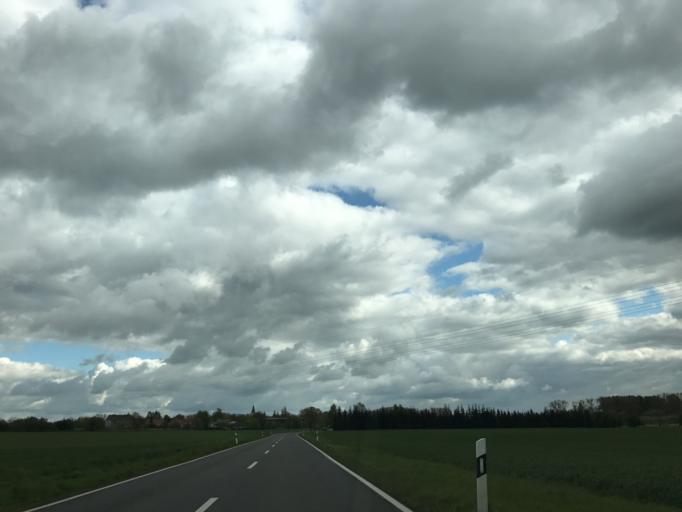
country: DE
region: Brandenburg
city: Wustermark
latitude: 52.5650
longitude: 12.9568
